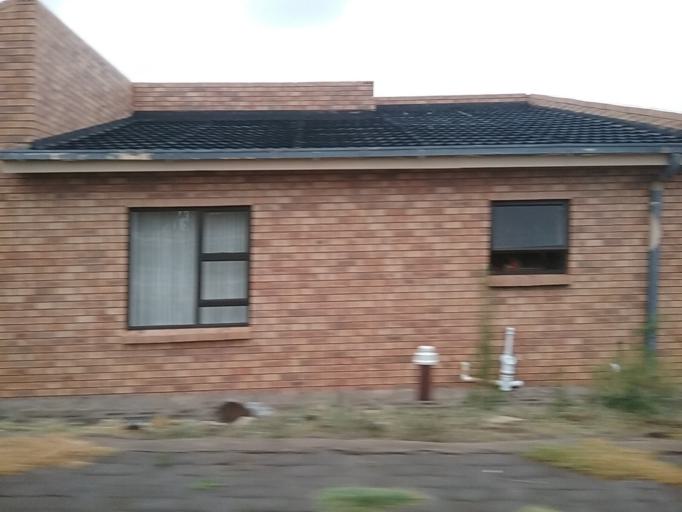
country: LS
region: Berea
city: Teyateyaneng
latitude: -29.1413
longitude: 27.7373
